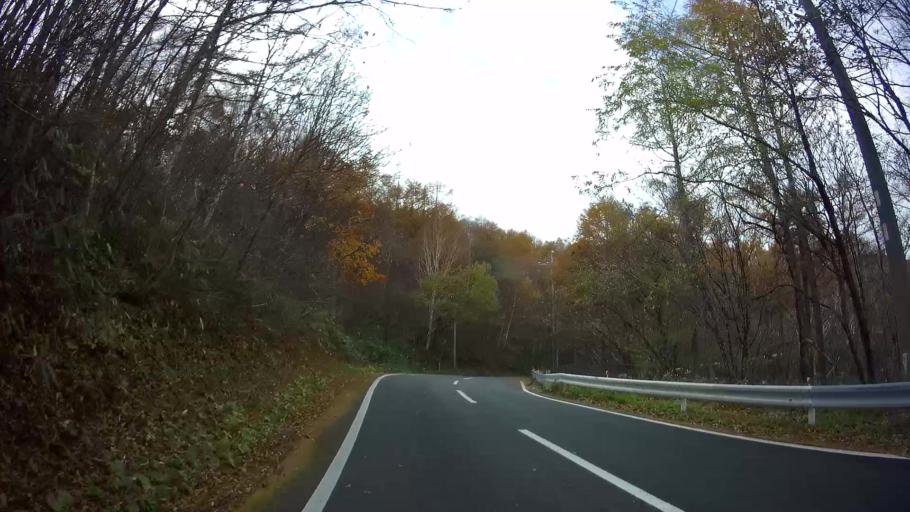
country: JP
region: Gunma
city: Nakanojomachi
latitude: 36.6751
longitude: 138.6657
